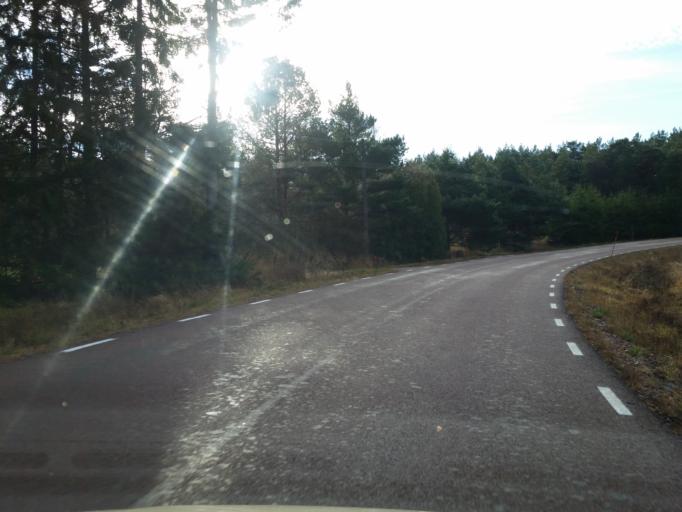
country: AX
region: Alands skaergard
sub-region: Kumlinge
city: Kumlinge
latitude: 60.2725
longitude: 20.7945
